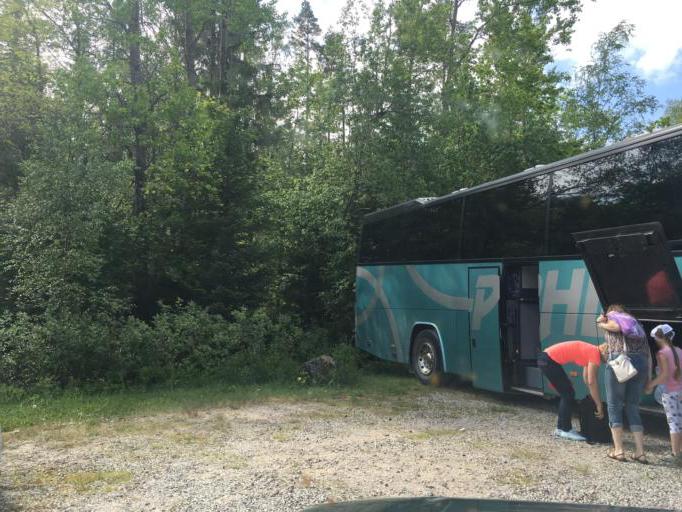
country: LV
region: Talsu Rajons
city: Valdemarpils
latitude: 57.3717
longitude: 22.5269
